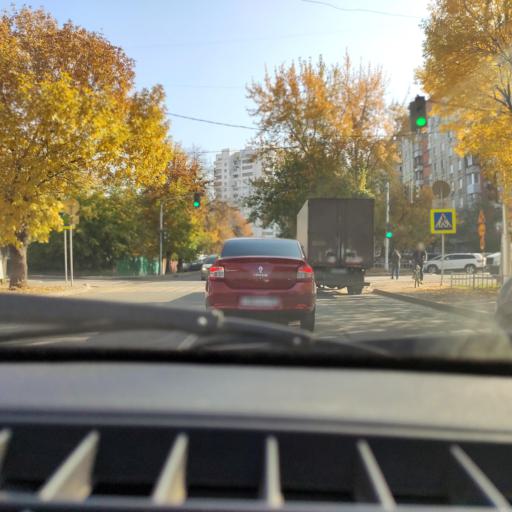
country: RU
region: Bashkortostan
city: Ufa
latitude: 54.7573
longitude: 56.0185
